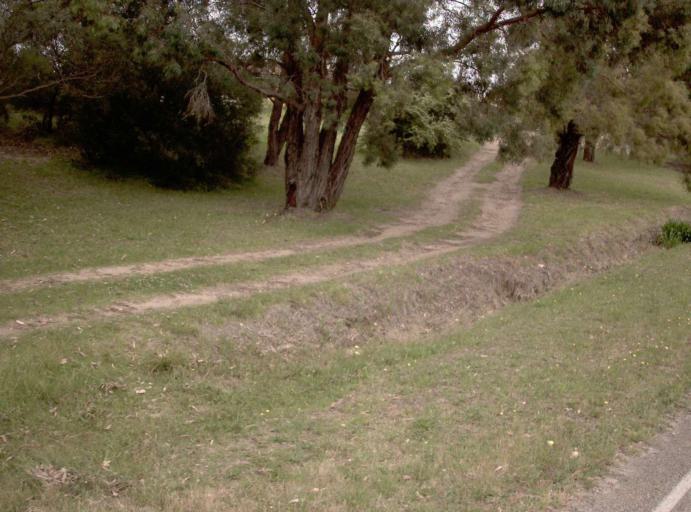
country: AU
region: Victoria
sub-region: East Gippsland
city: Bairnsdale
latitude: -37.8086
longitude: 147.6192
